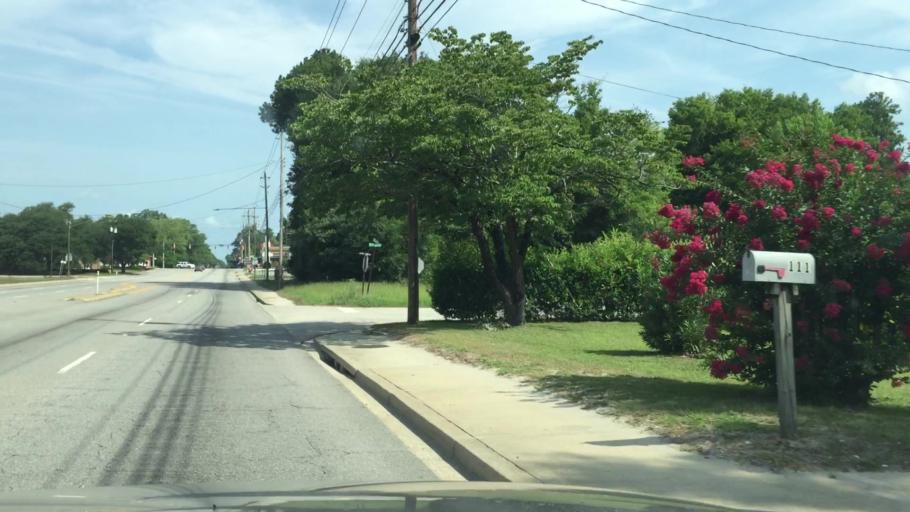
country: US
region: South Carolina
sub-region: Sumter County
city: Sumter
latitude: 33.9180
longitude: -80.3581
